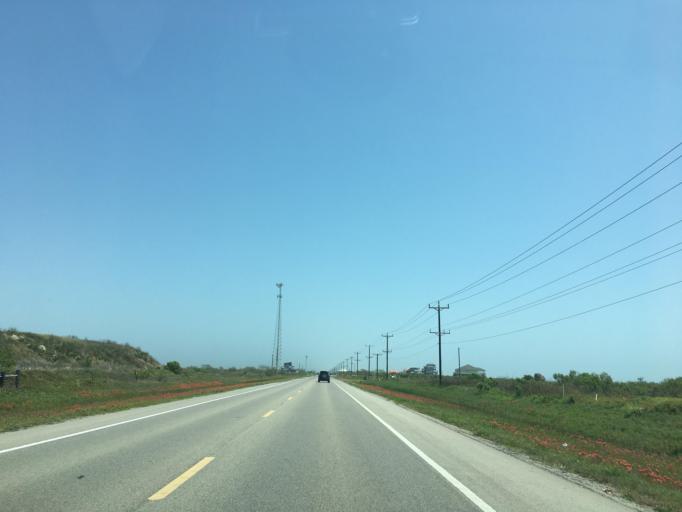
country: US
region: Texas
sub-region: Galveston County
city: Bolivar Peninsula
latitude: 29.4897
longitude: -94.5515
